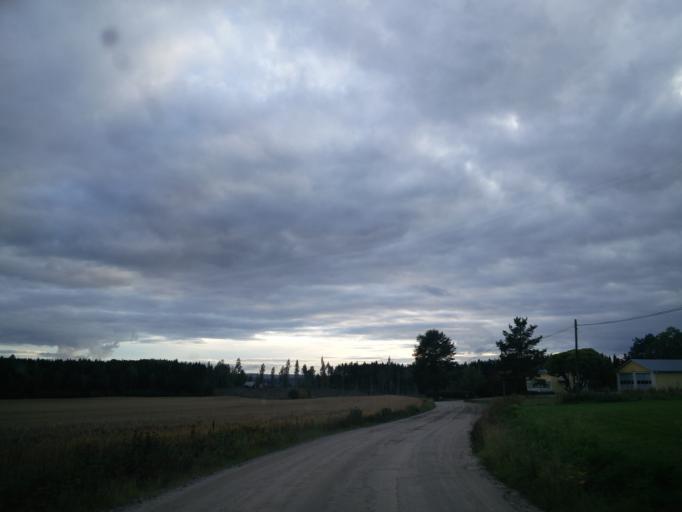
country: SE
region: Vaesternorrland
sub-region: Sundsvalls Kommun
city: Matfors
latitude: 62.3414
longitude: 17.0731
